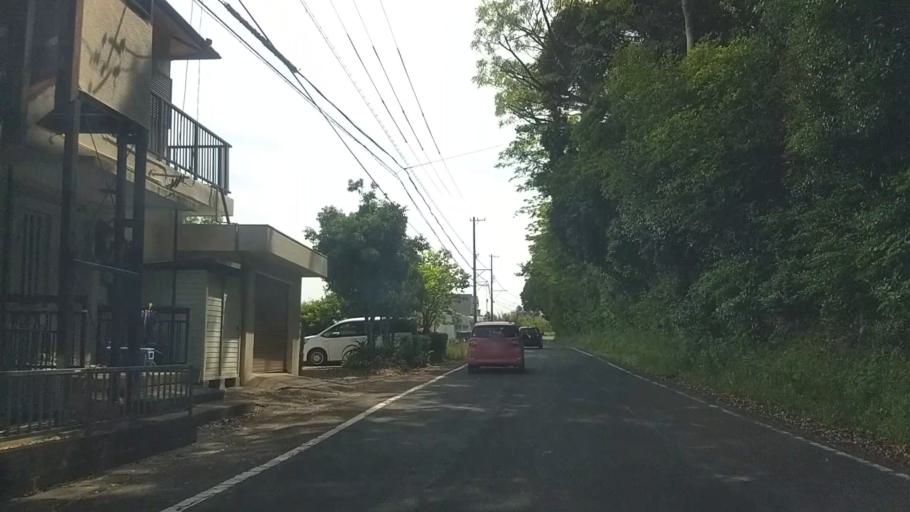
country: JP
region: Shizuoka
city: Kosai-shi
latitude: 34.7747
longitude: 137.5687
